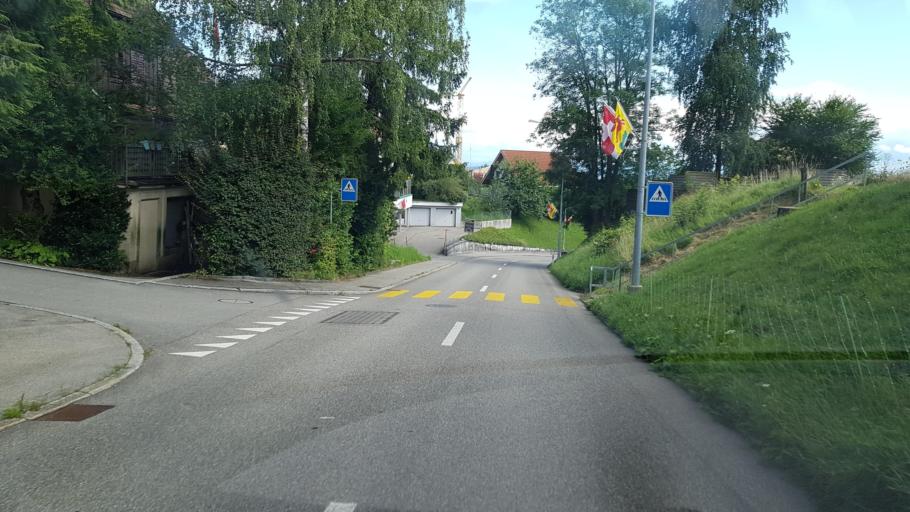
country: CH
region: Solothurn
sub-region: Bezirk Lebern
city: Riedholz
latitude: 47.2573
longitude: 7.5772
